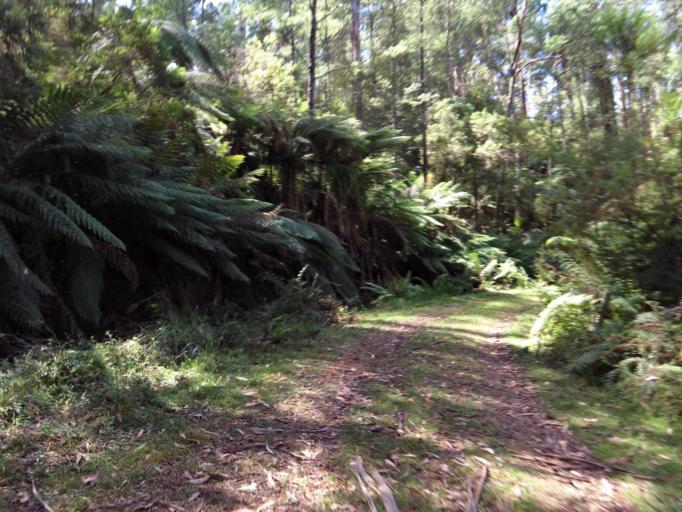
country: AU
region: Victoria
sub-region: Yarra Ranges
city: Millgrove
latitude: -37.6975
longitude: 145.7970
